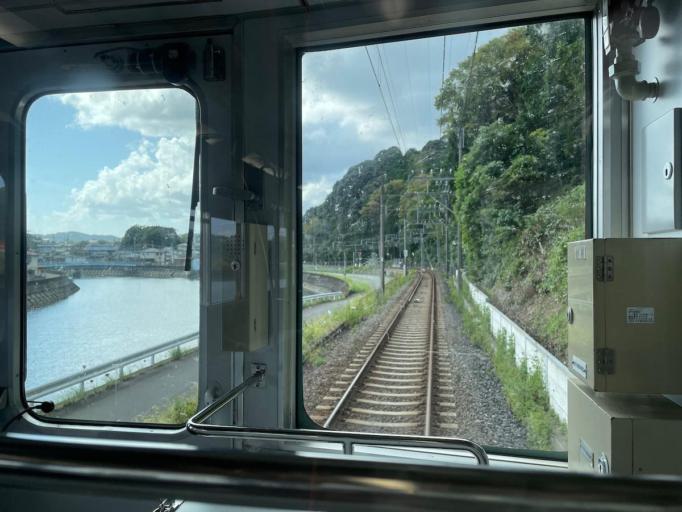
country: JP
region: Mie
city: Toba
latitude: 34.4597
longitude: 136.8411
